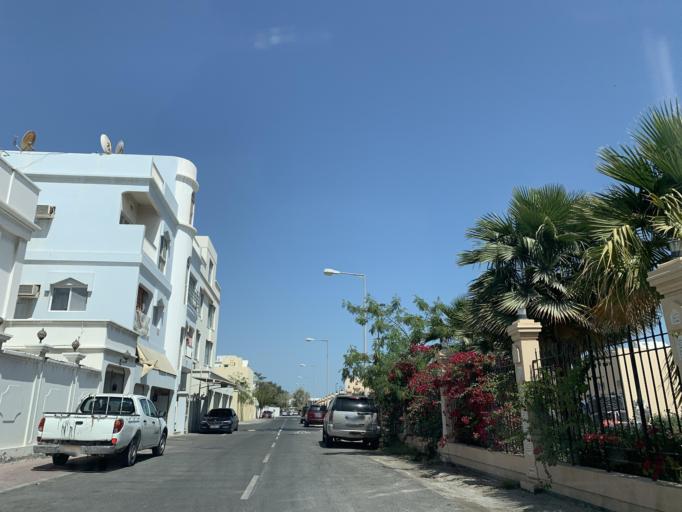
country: BH
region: Muharraq
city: Al Muharraq
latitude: 26.2656
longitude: 50.6198
